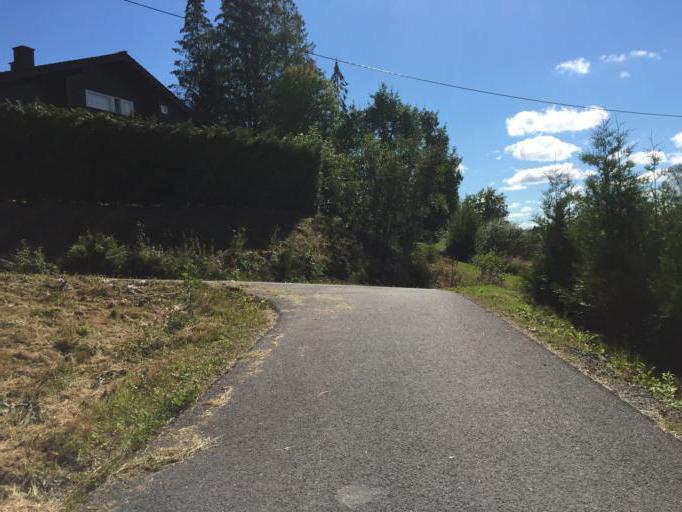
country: NO
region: Hedmark
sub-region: Kongsvinger
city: Kongsvinger
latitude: 60.2055
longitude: 11.9773
